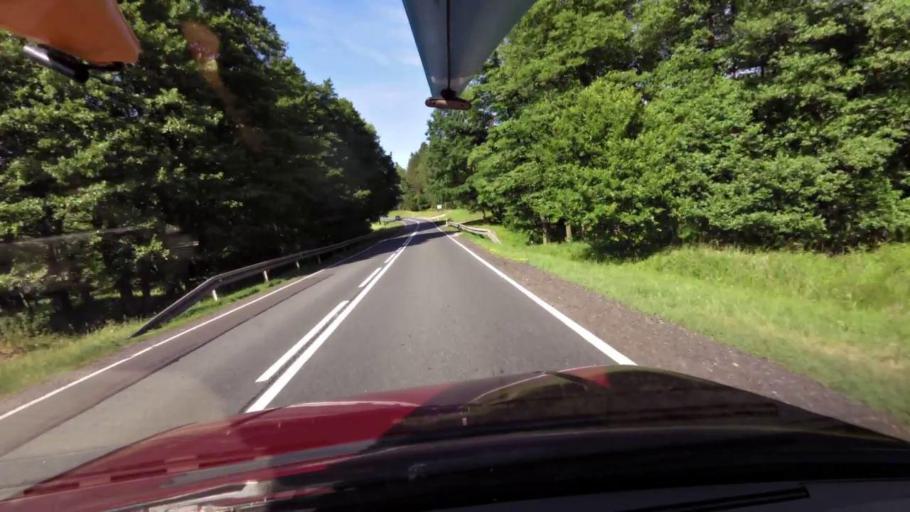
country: PL
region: Pomeranian Voivodeship
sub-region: Powiat bytowski
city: Miastko
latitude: 54.1132
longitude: 16.9977
